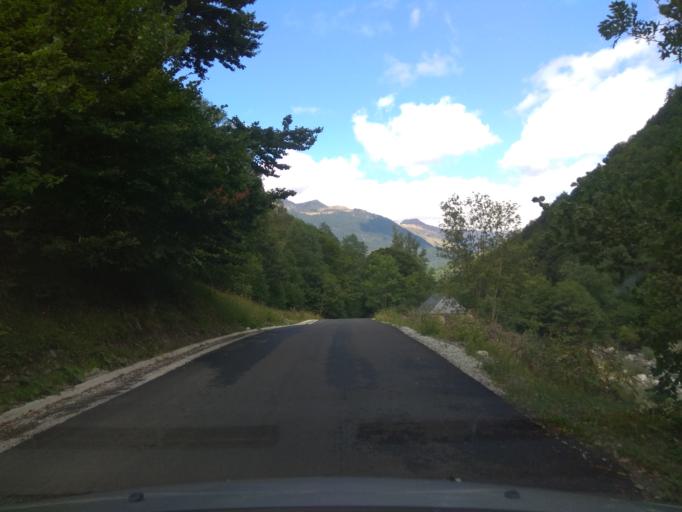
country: ES
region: Catalonia
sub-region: Provincia de Lleida
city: Vielha
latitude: 42.7110
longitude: 0.7188
